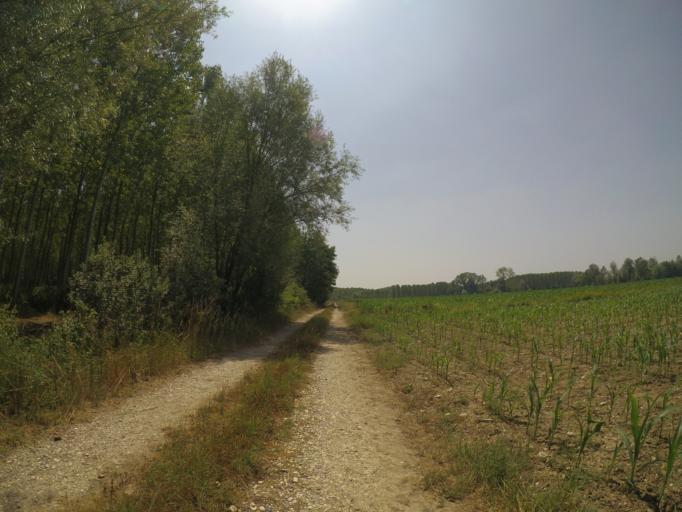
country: IT
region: Friuli Venezia Giulia
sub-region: Provincia di Udine
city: Bertiolo
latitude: 45.9227
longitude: 13.0535
